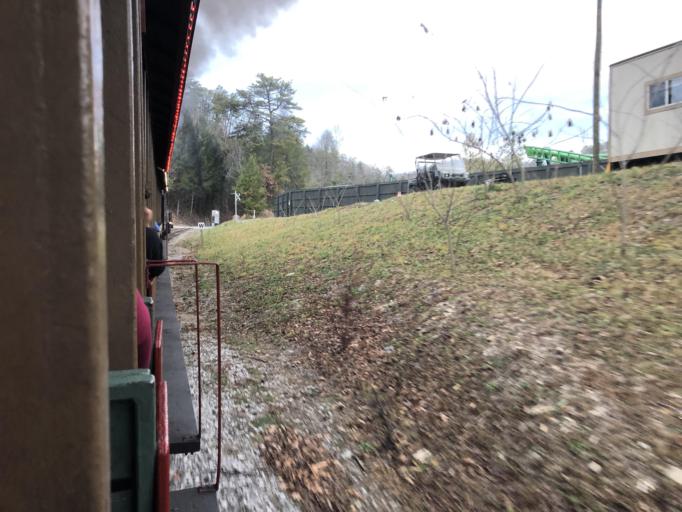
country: US
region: Tennessee
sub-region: Sevier County
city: Pigeon Forge
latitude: 35.7976
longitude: -83.5317
